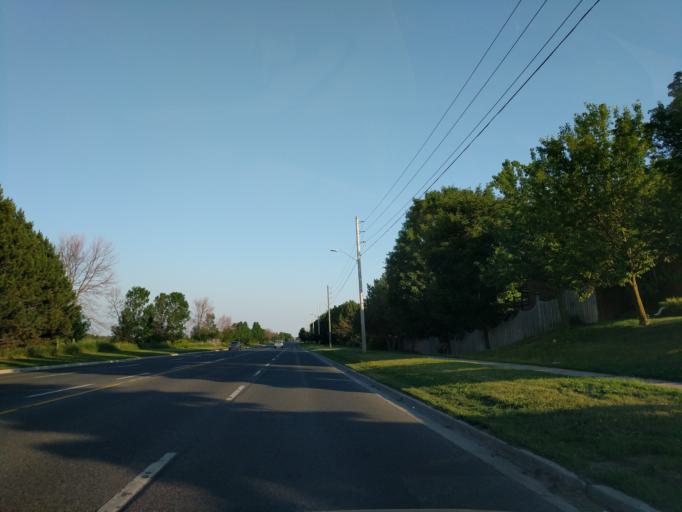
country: CA
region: Ontario
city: Oshawa
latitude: 43.9179
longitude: -78.9047
